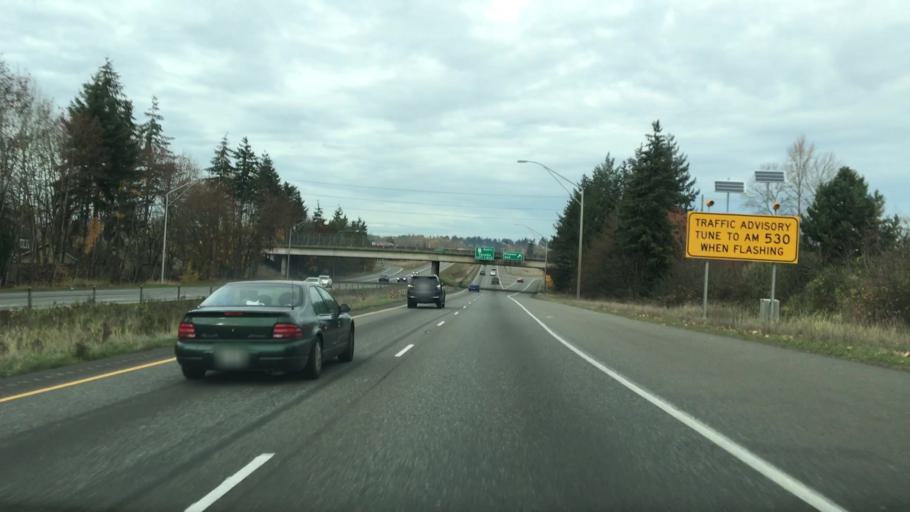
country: US
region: Washington
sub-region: Pierce County
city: Puyallup
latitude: 47.1847
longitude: -122.2829
